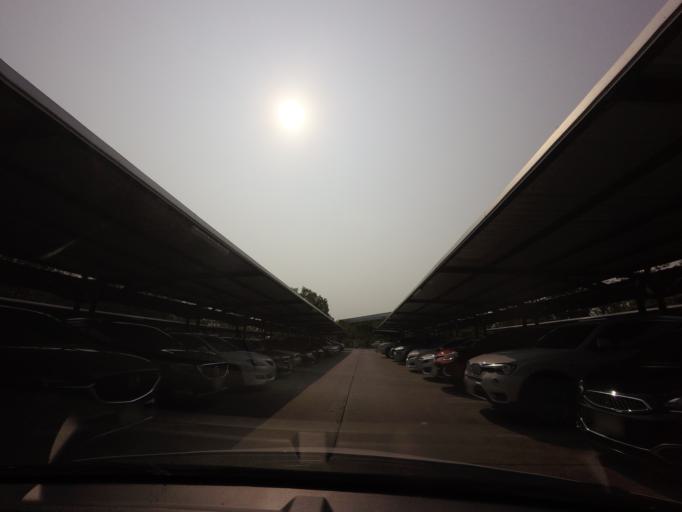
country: TH
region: Nakhon Pathom
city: Salaya
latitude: 13.7921
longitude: 100.3177
